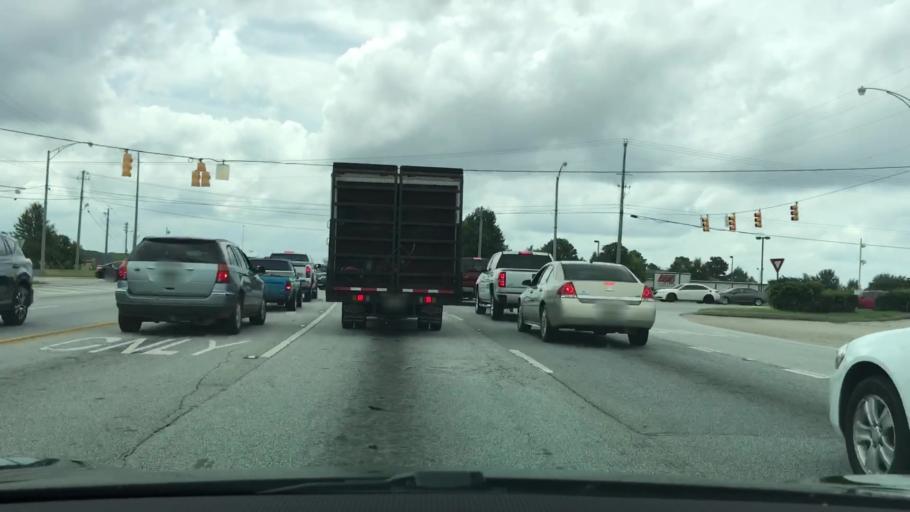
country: US
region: Alabama
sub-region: Lee County
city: Opelika
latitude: 32.6232
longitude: -85.4051
